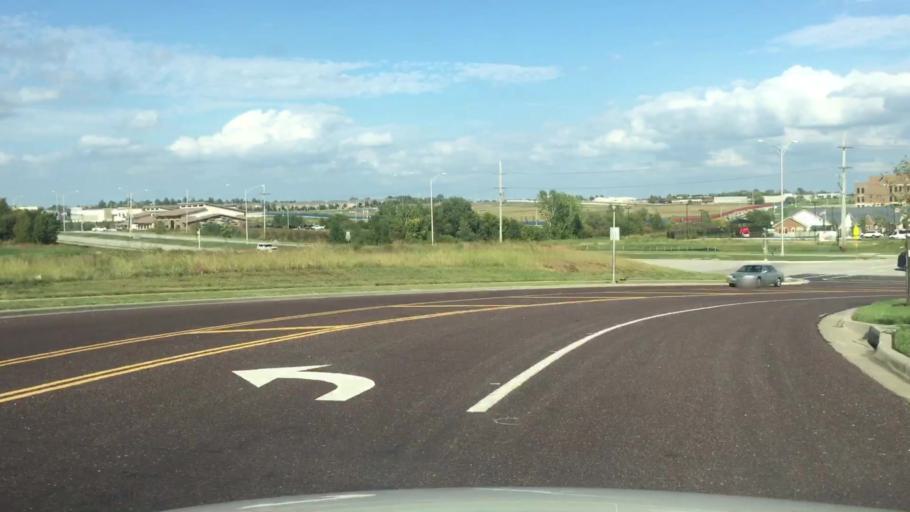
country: US
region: Kansas
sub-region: Johnson County
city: Lenexa
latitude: 38.8306
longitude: -94.6874
